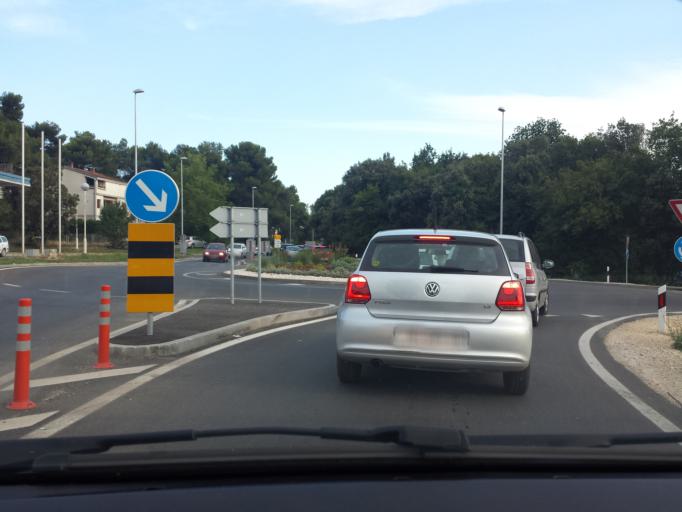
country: HR
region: Istarska
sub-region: Grad Pula
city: Pula
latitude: 44.8929
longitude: 13.8460
